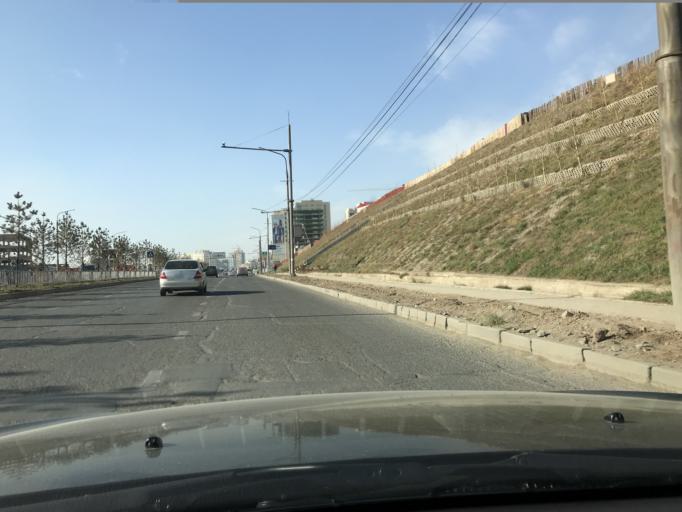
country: MN
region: Ulaanbaatar
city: Ulaanbaatar
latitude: 47.9265
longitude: 106.9001
